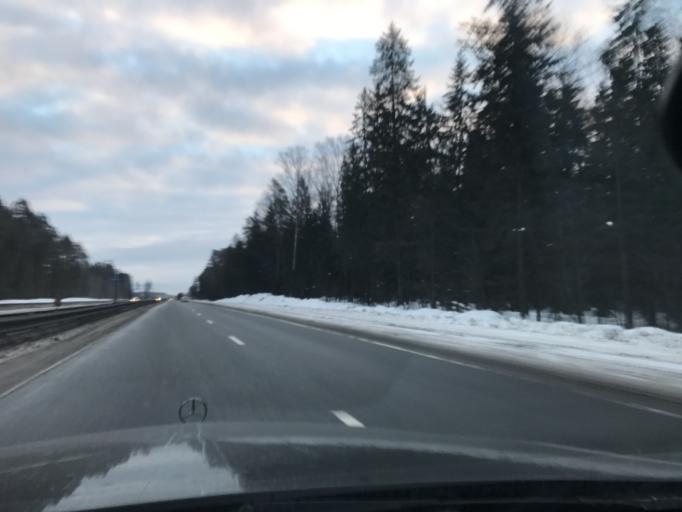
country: RU
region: Vladimir
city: Stepantsevo
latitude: 56.2322
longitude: 41.7792
